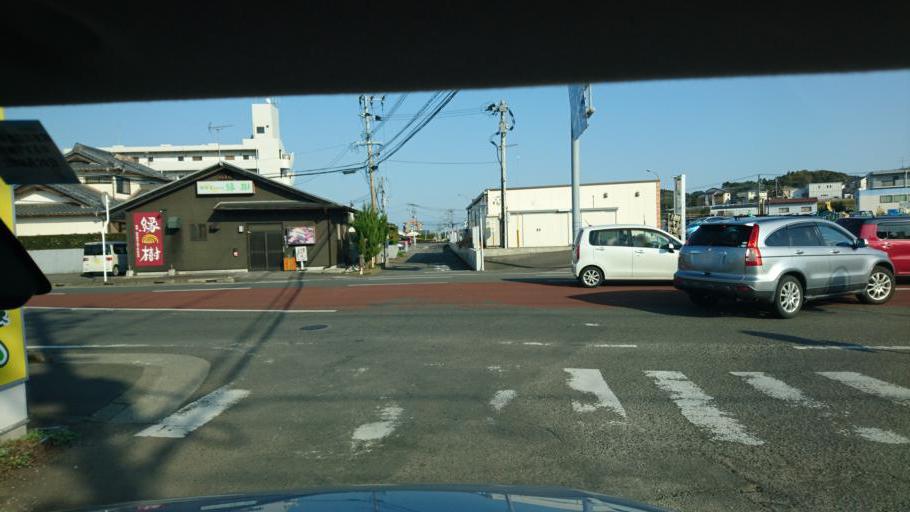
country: JP
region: Miyazaki
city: Miyazaki-shi
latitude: 31.9748
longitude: 131.4399
